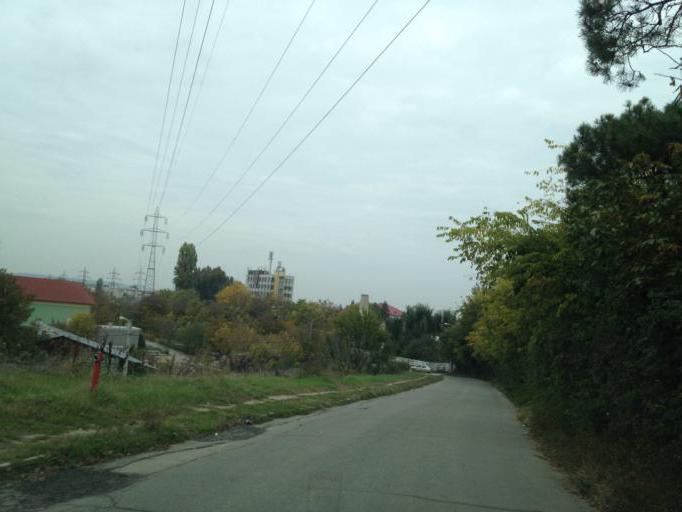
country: RO
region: Dolj
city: Craiova
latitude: 44.2947
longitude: 23.8048
